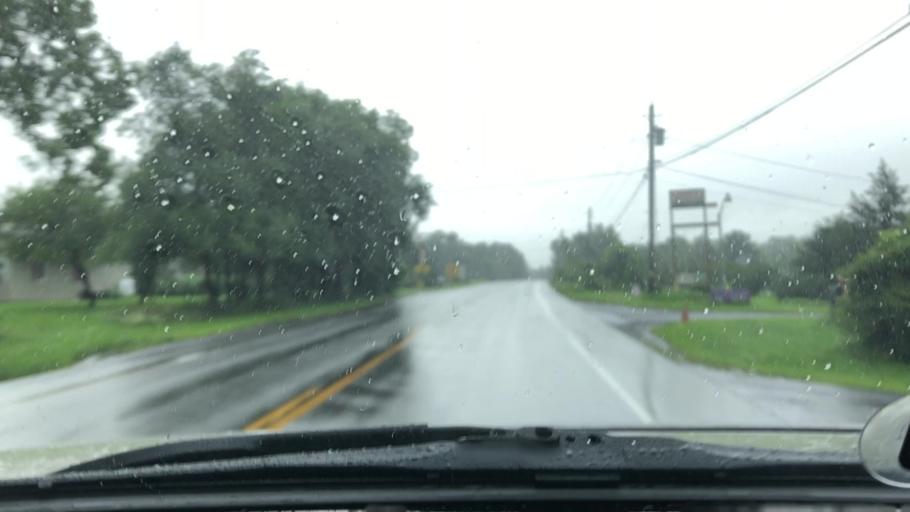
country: US
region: New York
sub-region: Greene County
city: Palenville
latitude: 42.2117
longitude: -73.9851
